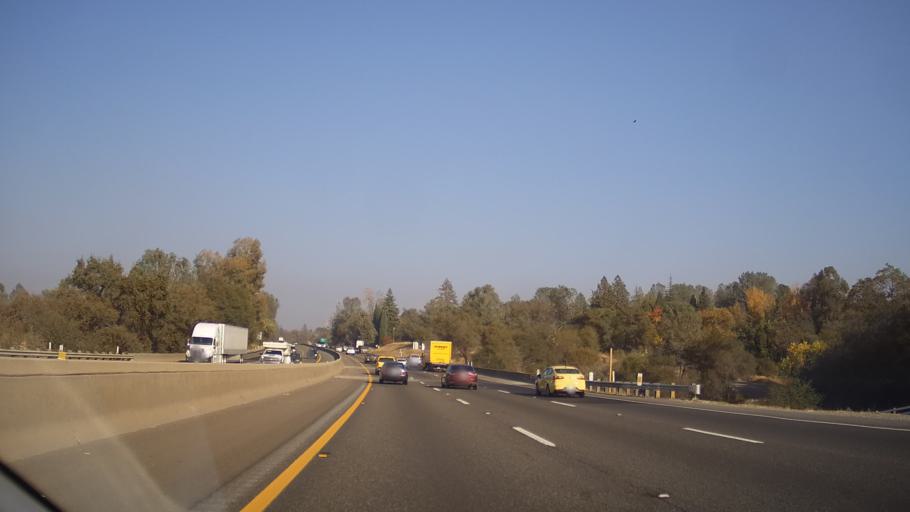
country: US
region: California
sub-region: Placer County
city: Newcastle
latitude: 38.8824
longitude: -121.1051
